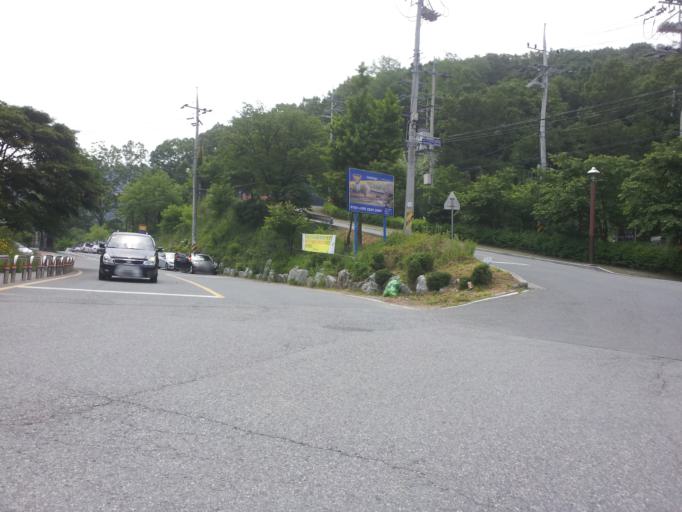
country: KR
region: Daejeon
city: Daejeon
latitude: 36.3311
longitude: 127.4805
